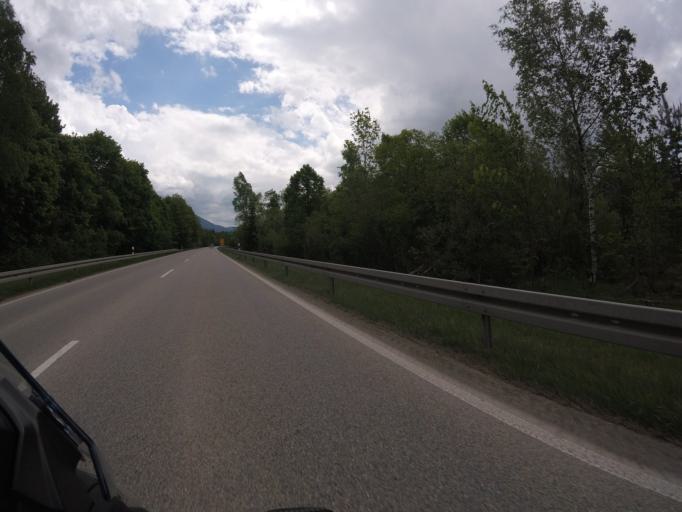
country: DE
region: Bavaria
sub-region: Upper Bavaria
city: Lenggries
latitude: 47.6883
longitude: 11.5695
